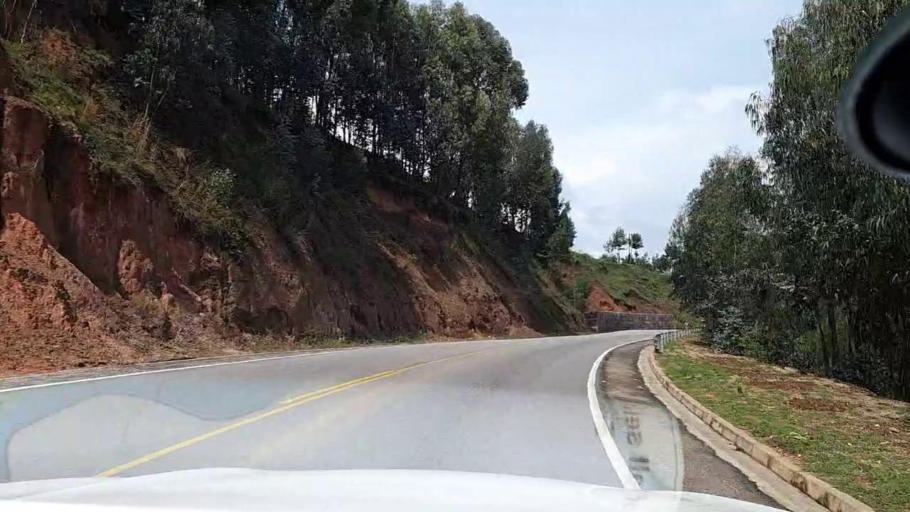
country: RW
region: Southern Province
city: Nzega
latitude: -2.4931
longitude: 29.5088
